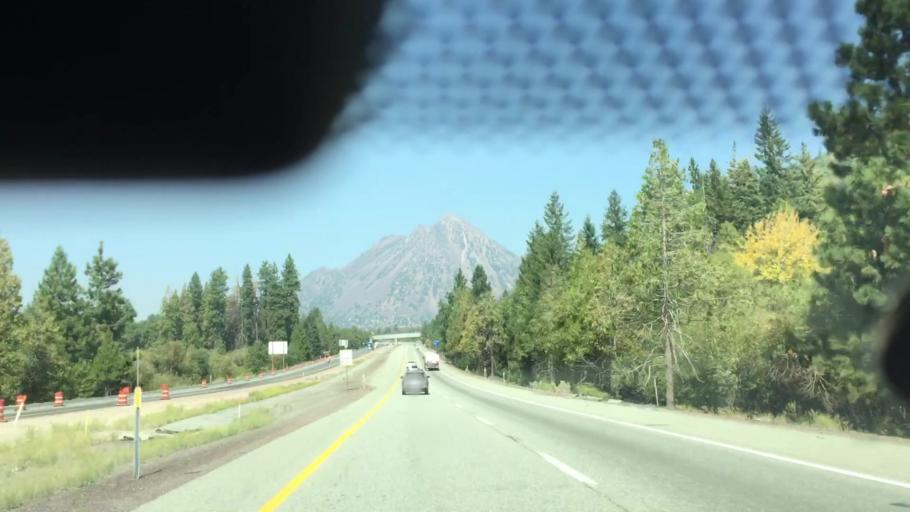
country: US
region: California
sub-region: Siskiyou County
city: Mount Shasta
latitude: 41.3244
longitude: -122.3278
